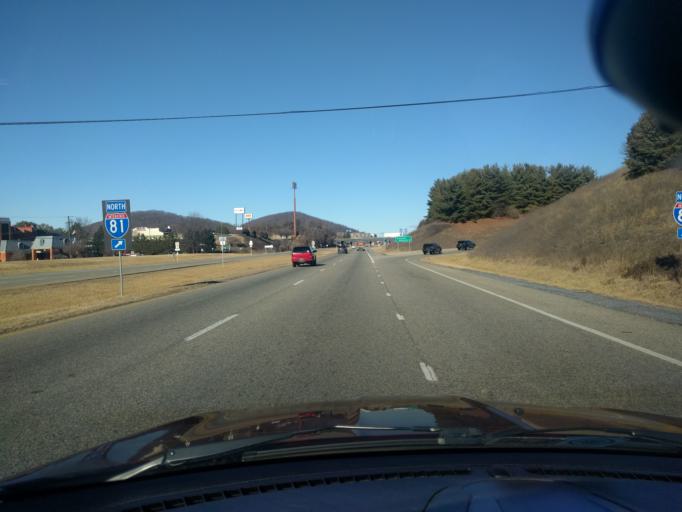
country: US
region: Virginia
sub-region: Augusta County
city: Jolivue
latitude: 38.1258
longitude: -79.0327
